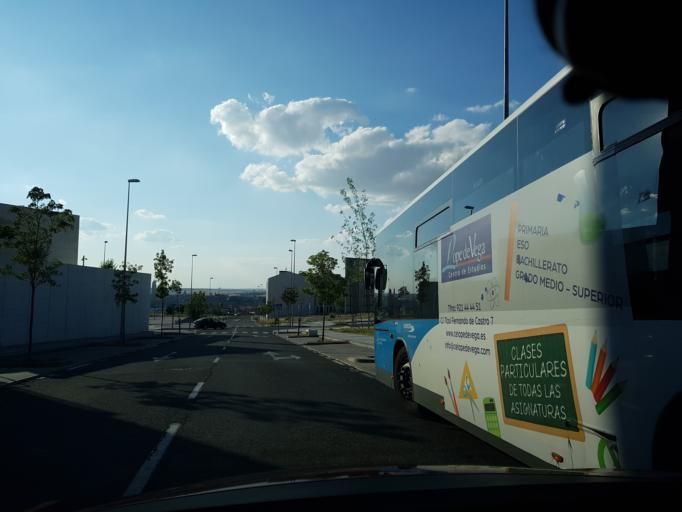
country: ES
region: Castille and Leon
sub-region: Provincia de Segovia
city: Segovia
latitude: 40.9362
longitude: -4.1034
